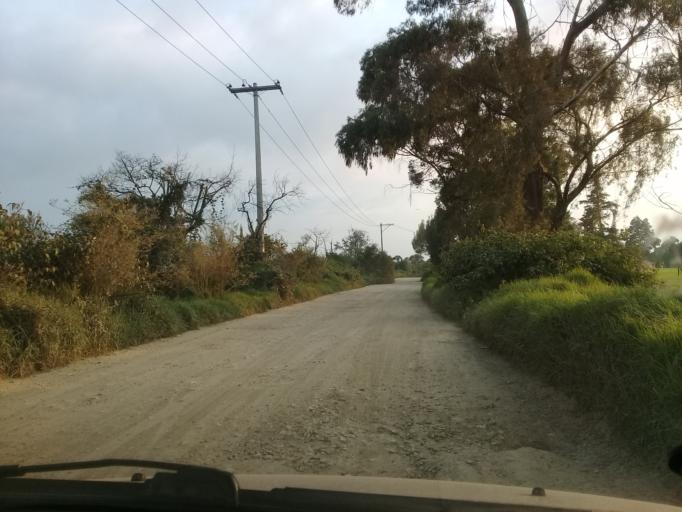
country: CO
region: Cundinamarca
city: El Rosal
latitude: 4.7949
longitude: -74.2259
